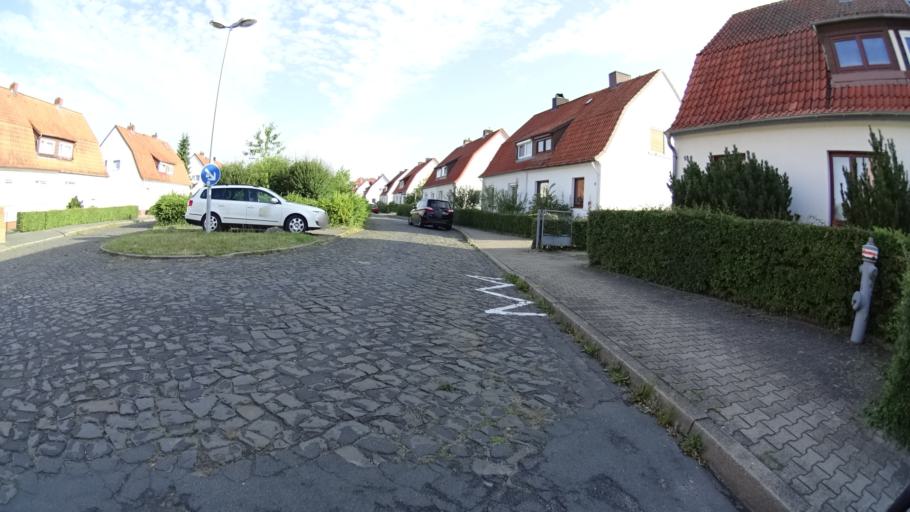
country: DE
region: Lower Saxony
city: Lueneburg
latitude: 53.2384
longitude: 10.3910
